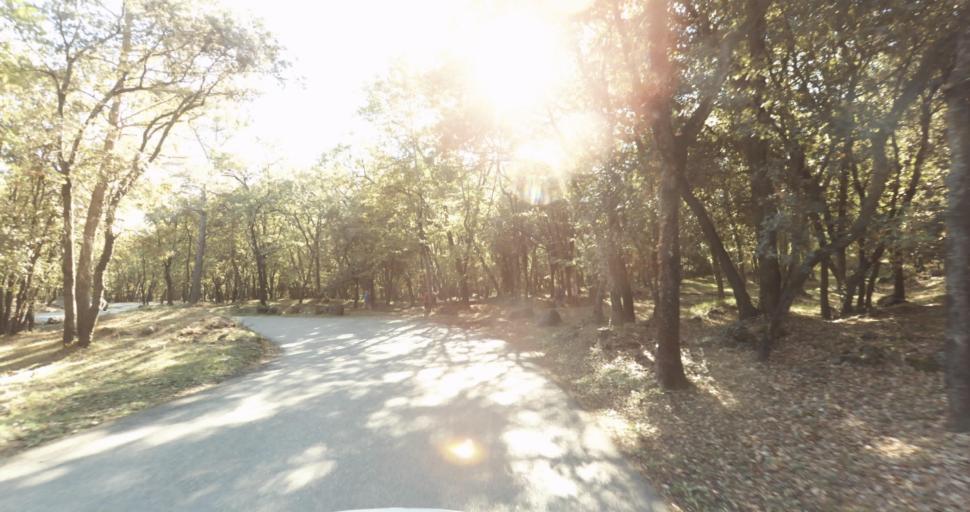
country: FR
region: Provence-Alpes-Cote d'Azur
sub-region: Departement des Alpes-Maritimes
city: Vence
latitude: 43.7129
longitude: 7.0968
